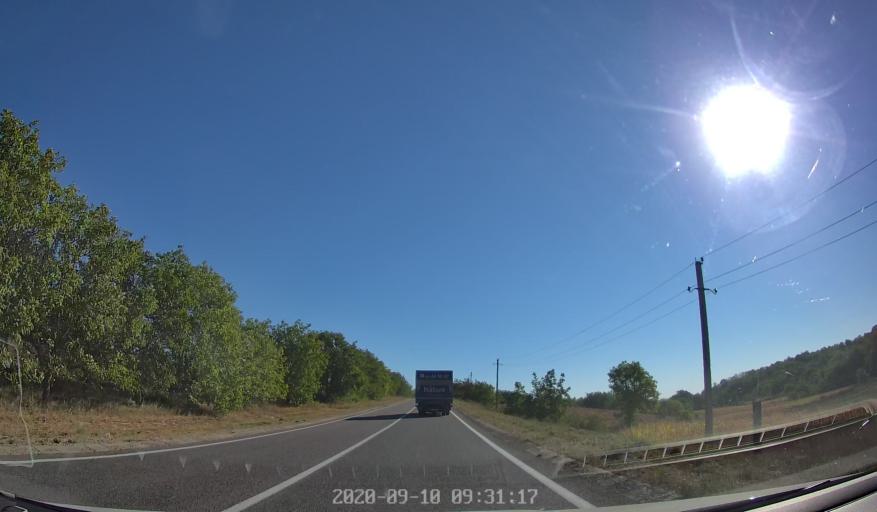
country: MD
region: Soldanesti
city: Soldanesti
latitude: 47.7022
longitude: 28.8385
